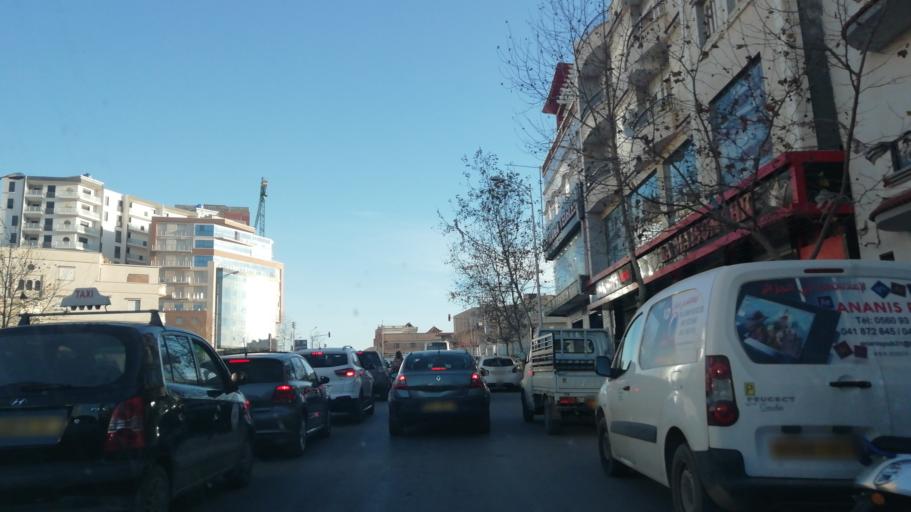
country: DZ
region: Oran
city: Bir el Djir
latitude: 35.7214
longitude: -0.5835
